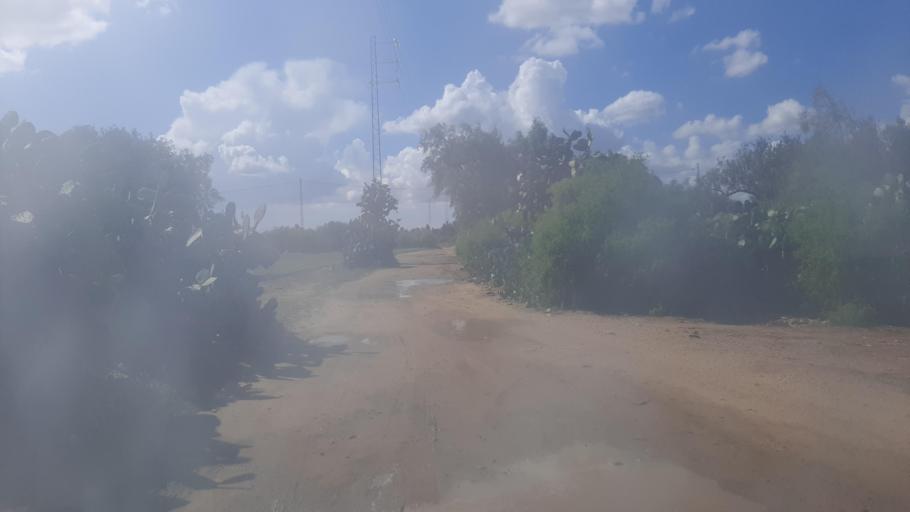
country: TN
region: Nabul
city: Korba
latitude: 36.6248
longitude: 10.8600
